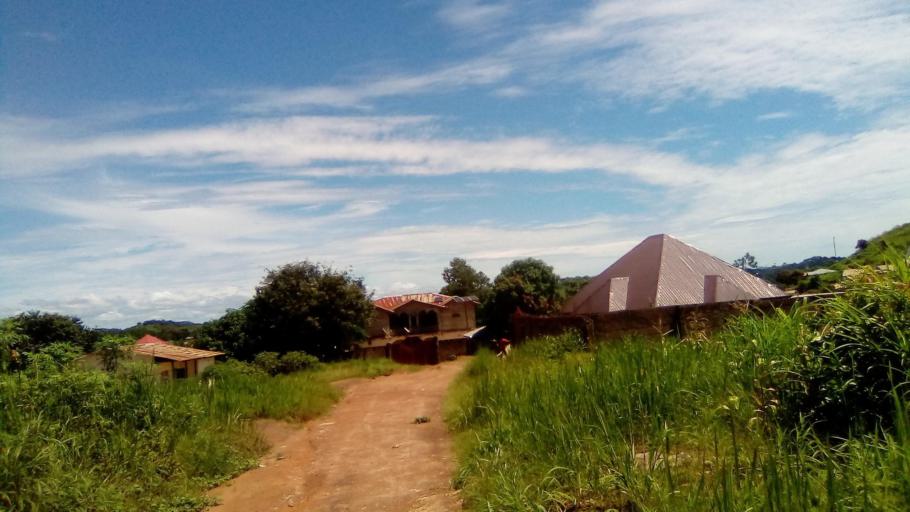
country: SL
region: Eastern Province
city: Simbakoro
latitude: 8.6321
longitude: -10.9982
